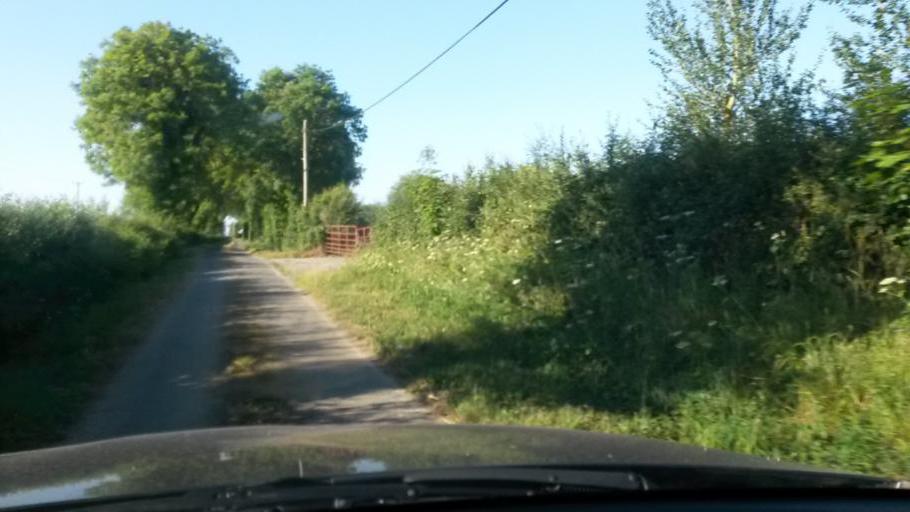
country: IE
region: Leinster
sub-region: Dublin City
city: Finglas
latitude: 53.4418
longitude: -6.3186
